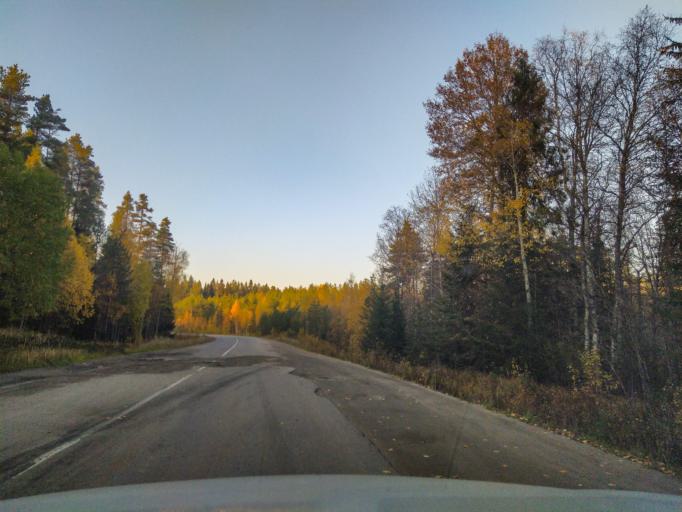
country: RU
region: Republic of Karelia
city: Lakhdenpokh'ya
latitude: 61.3669
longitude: 29.9844
